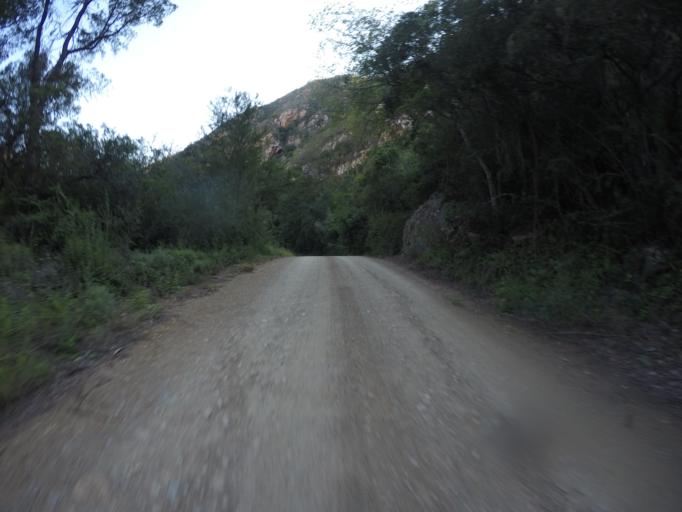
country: ZA
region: Eastern Cape
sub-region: Cacadu District Municipality
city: Kareedouw
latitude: -33.6592
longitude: 24.5349
